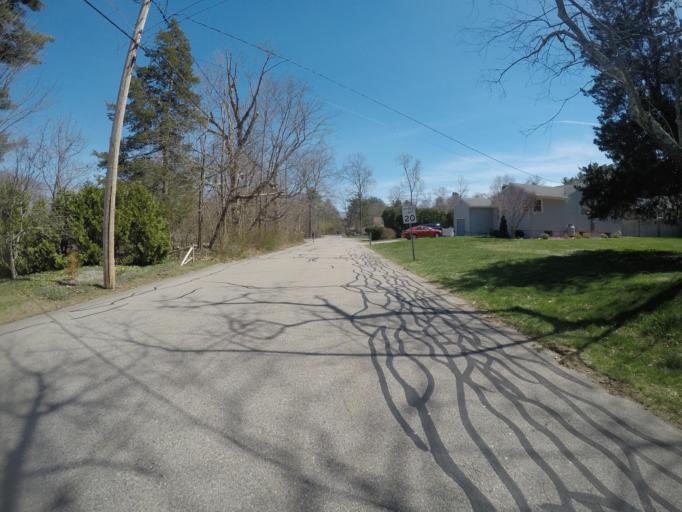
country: US
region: Massachusetts
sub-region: Bristol County
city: Easton
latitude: 42.0465
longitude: -71.0854
